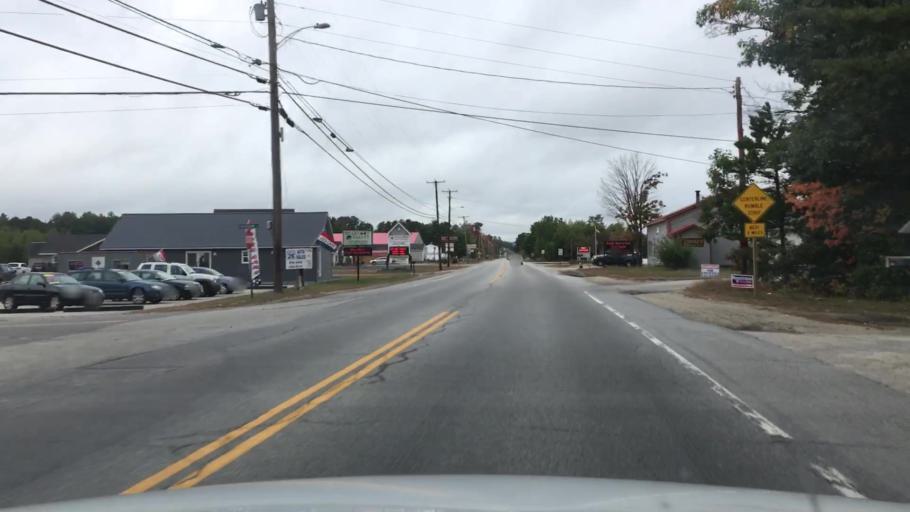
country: US
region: Maine
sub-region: Oxford County
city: Oxford
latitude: 44.1443
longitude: -70.4776
